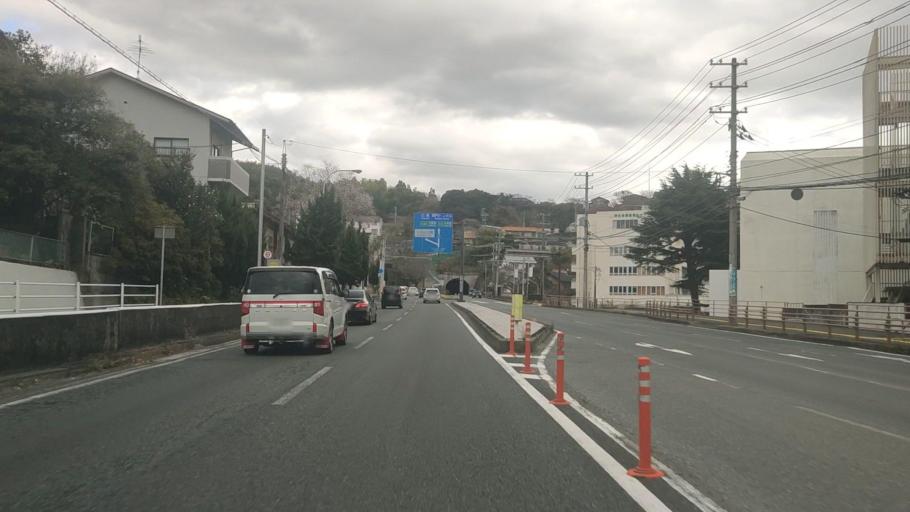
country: JP
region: Yamaguchi
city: Shimonoseki
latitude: 33.9687
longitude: 130.9411
